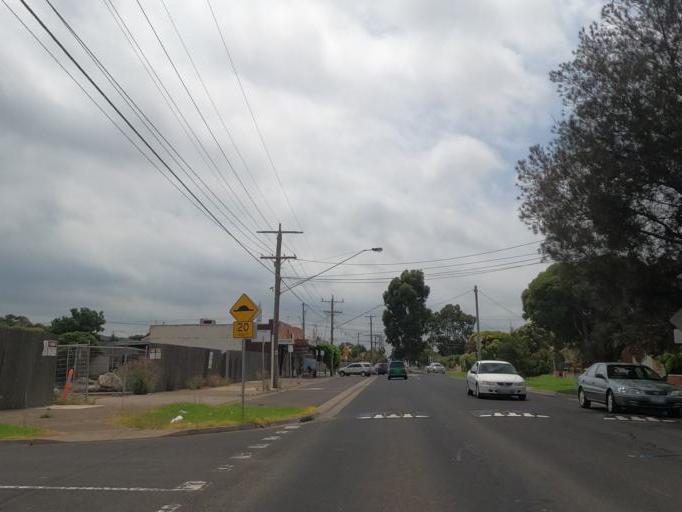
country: AU
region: Victoria
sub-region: Moreland
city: Glenroy
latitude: -37.6976
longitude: 144.9246
